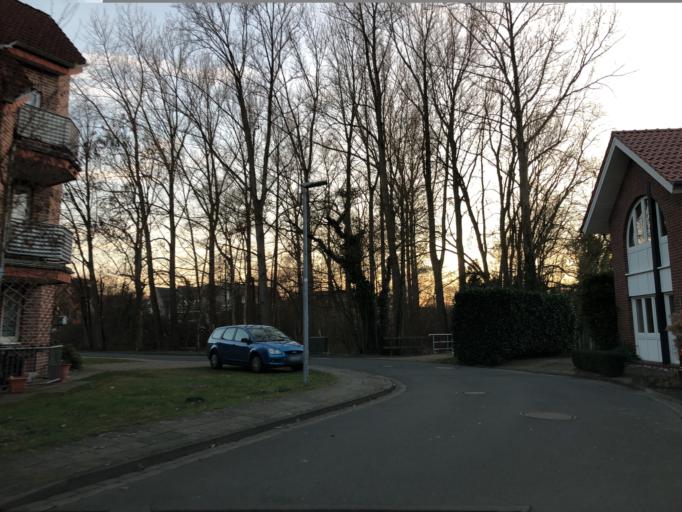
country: DE
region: Lower Saxony
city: Papenburg
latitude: 53.0792
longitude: 7.3871
